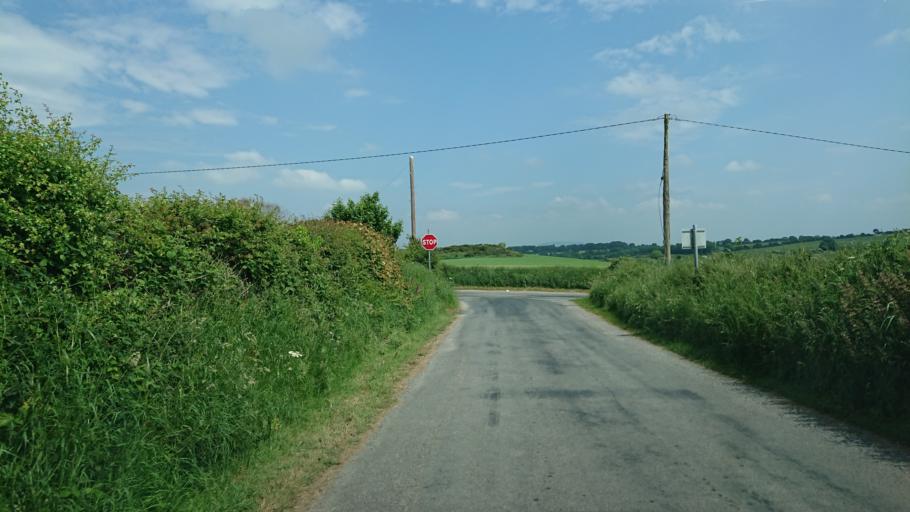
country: IE
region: Munster
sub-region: Waterford
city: Dunmore East
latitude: 52.2303
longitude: -7.0044
